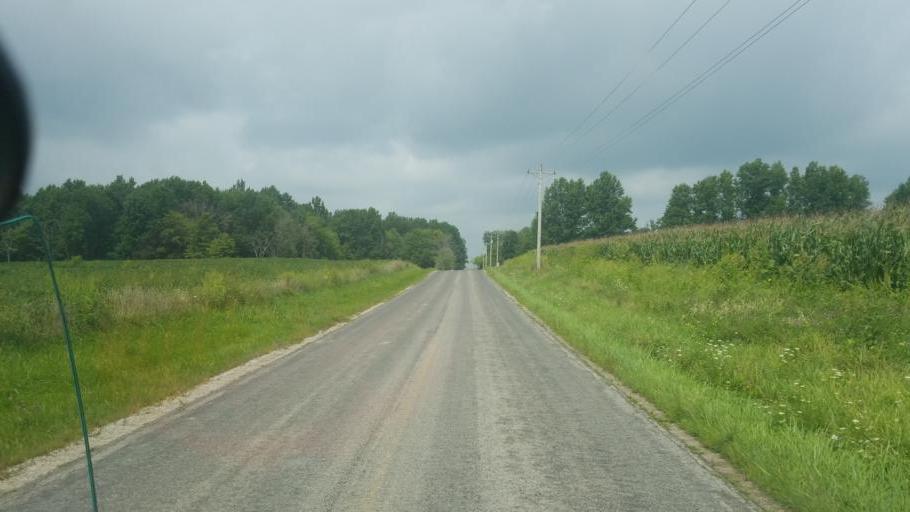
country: US
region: Ohio
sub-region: Huron County
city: Greenwich
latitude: 40.9877
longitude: -82.4770
